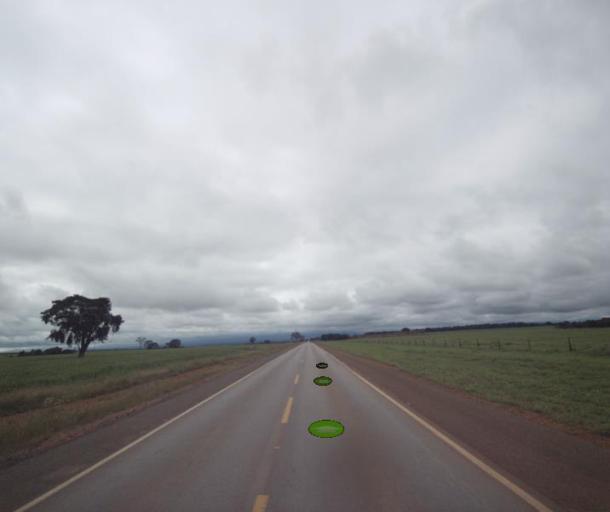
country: BR
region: Goias
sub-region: Uruacu
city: Uruacu
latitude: -14.6933
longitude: -49.1183
